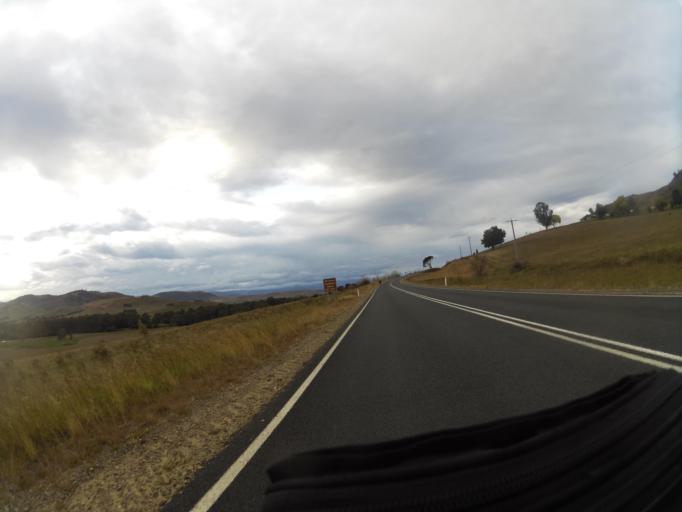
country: AU
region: New South Wales
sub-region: Snowy River
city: Jindabyne
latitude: -36.0827
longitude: 147.9768
